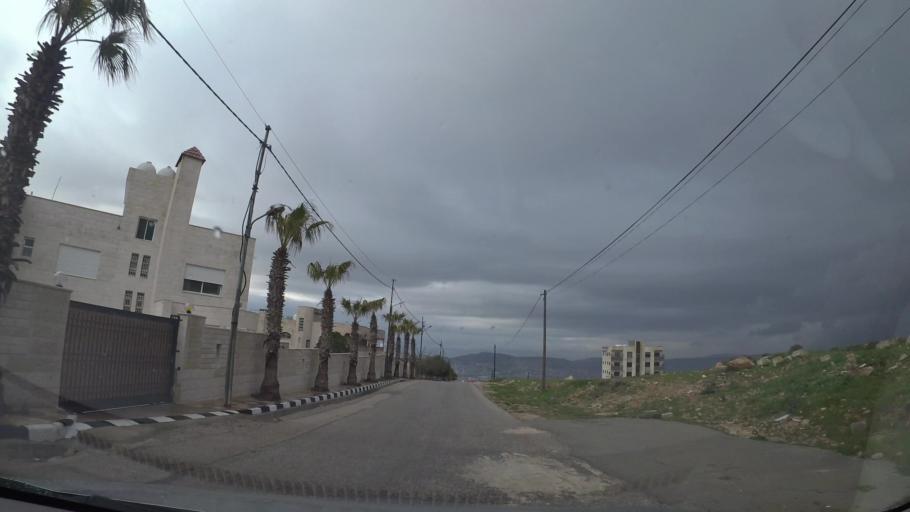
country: JO
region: Amman
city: Al Jubayhah
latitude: 32.0388
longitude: 35.8429
